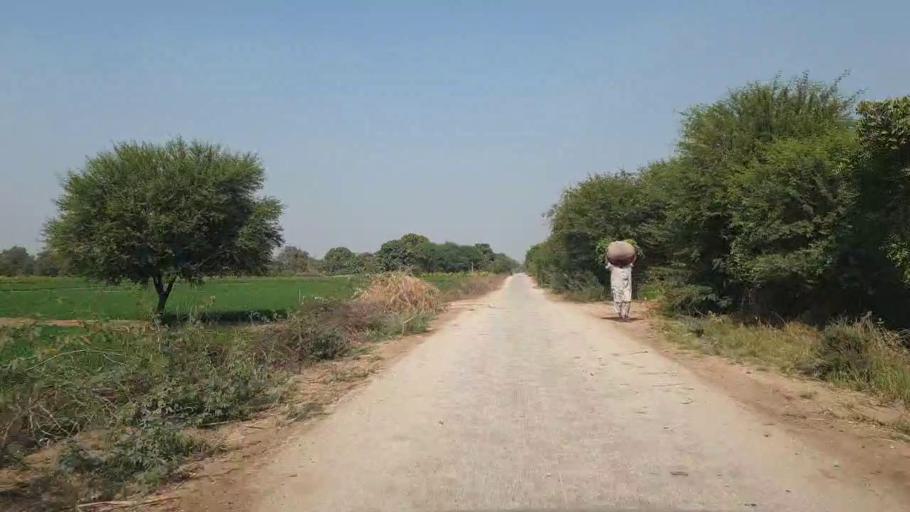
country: PK
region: Sindh
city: Chambar
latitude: 25.4070
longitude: 68.8878
